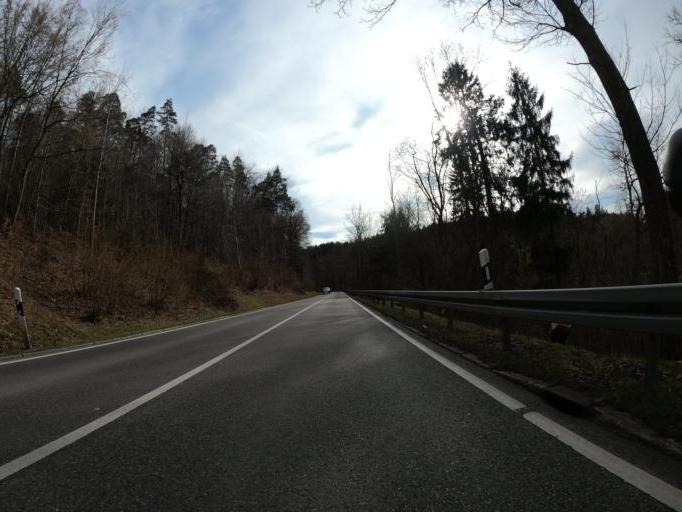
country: DE
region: Baden-Wuerttemberg
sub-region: Regierungsbezirk Stuttgart
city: Steinenbronn
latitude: 48.6818
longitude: 9.1289
